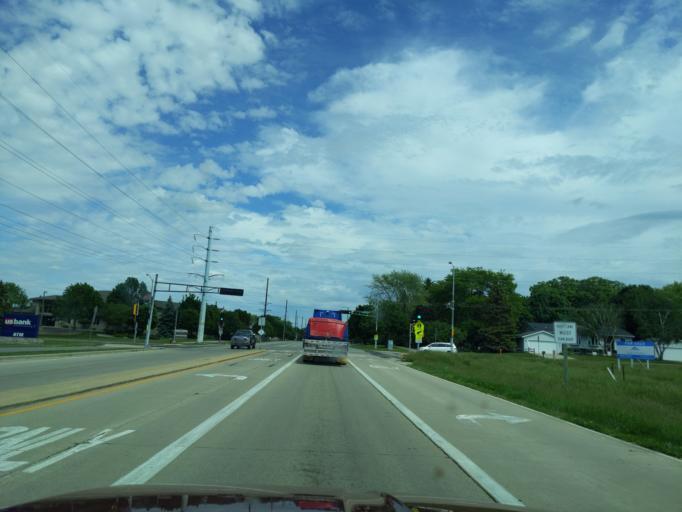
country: US
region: Wisconsin
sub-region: Dane County
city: Sun Prairie
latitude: 43.1871
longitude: -89.2553
